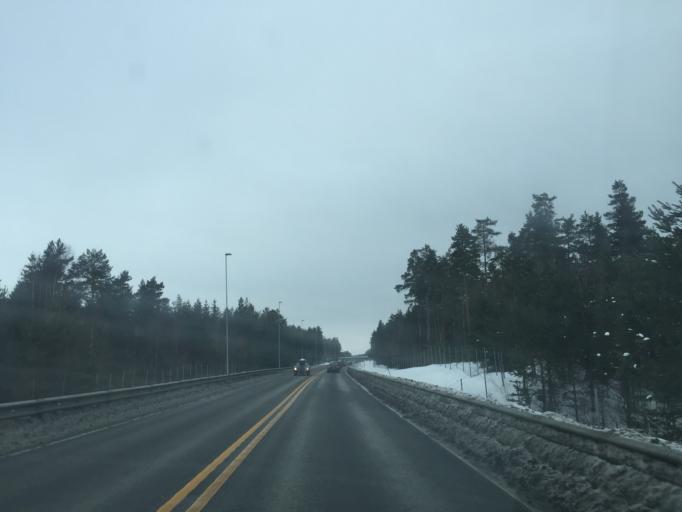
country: NO
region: Hedmark
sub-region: Loten
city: Loten
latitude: 60.7514
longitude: 11.3017
